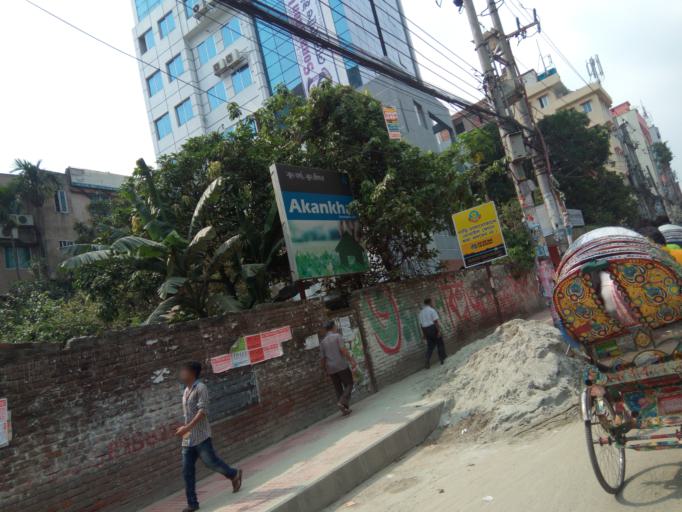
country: BD
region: Dhaka
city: Azimpur
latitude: 23.7522
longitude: 90.3876
